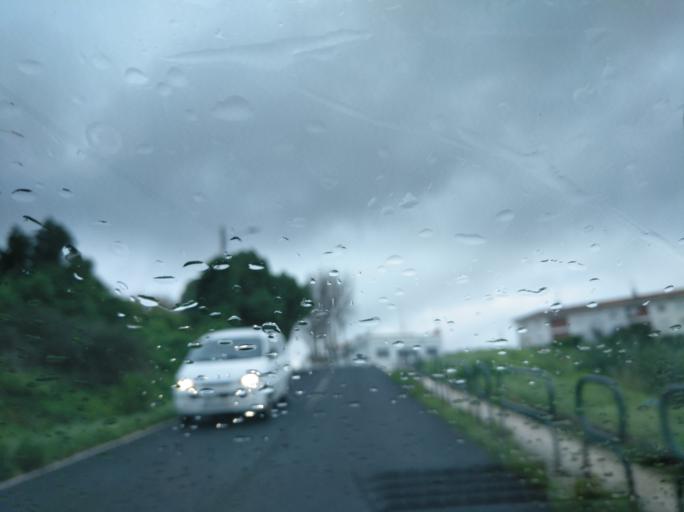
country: PT
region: Lisbon
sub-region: Odivelas
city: Pontinha
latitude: 38.7711
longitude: -9.1949
